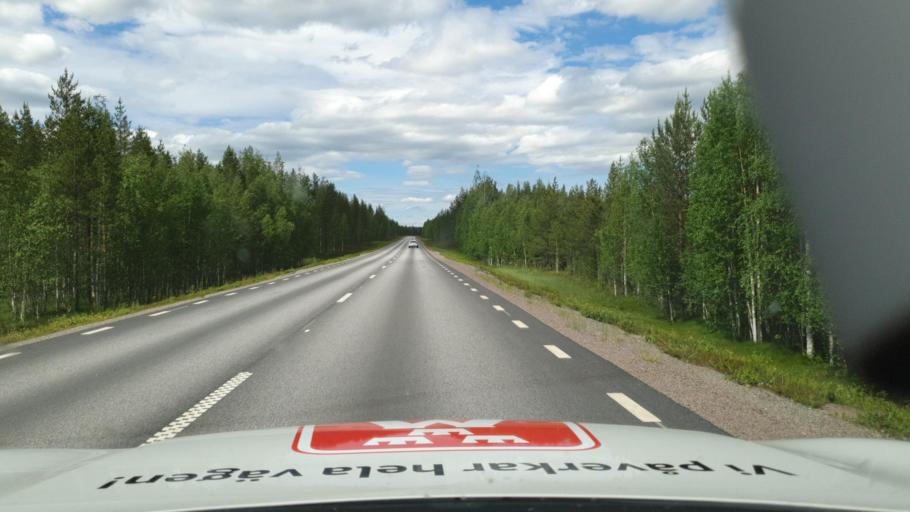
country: SE
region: Vaesterbotten
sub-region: Skelleftea Kommun
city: Langsele
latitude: 65.1359
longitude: 19.9117
